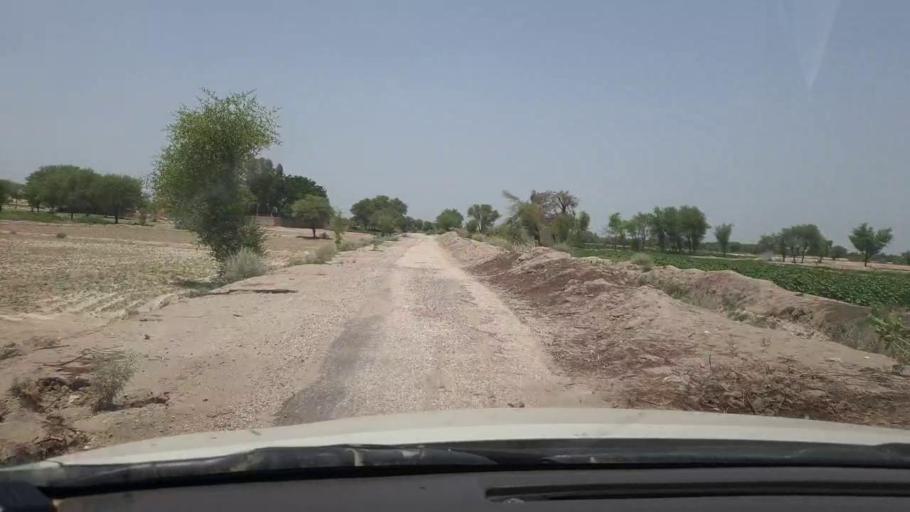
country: PK
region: Sindh
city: Rohri
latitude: 27.5072
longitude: 69.1805
